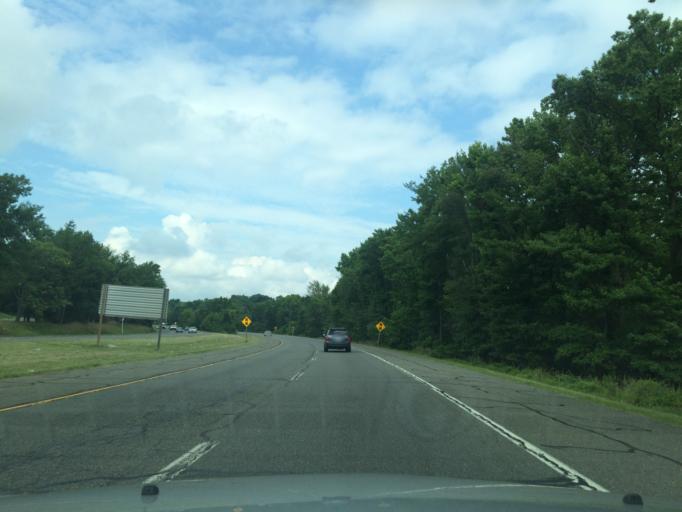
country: US
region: Maryland
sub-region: Prince George's County
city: Coral Hills
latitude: 38.8661
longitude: -76.9280
